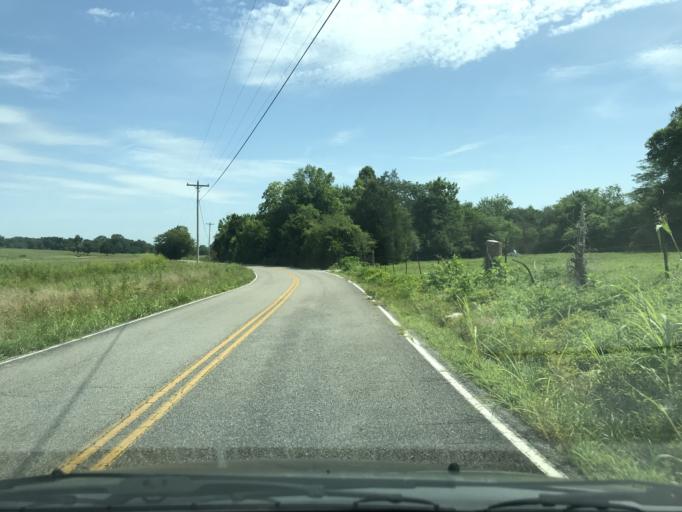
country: US
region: Tennessee
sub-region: Hamilton County
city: Lakesite
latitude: 35.2165
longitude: -85.0176
